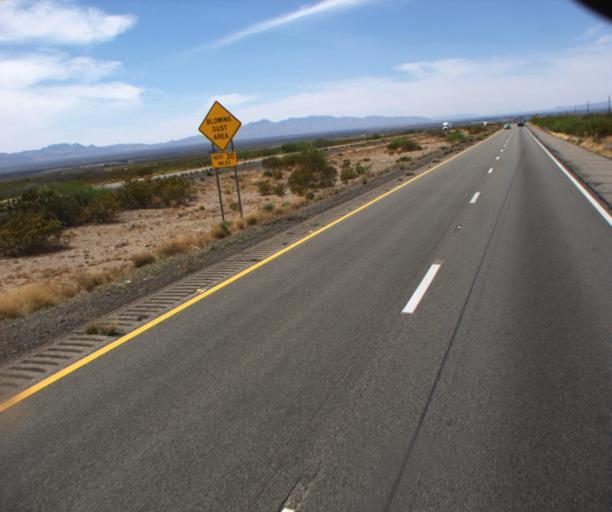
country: US
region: New Mexico
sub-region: Hidalgo County
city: Lordsburg
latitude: 32.2473
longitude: -109.1340
